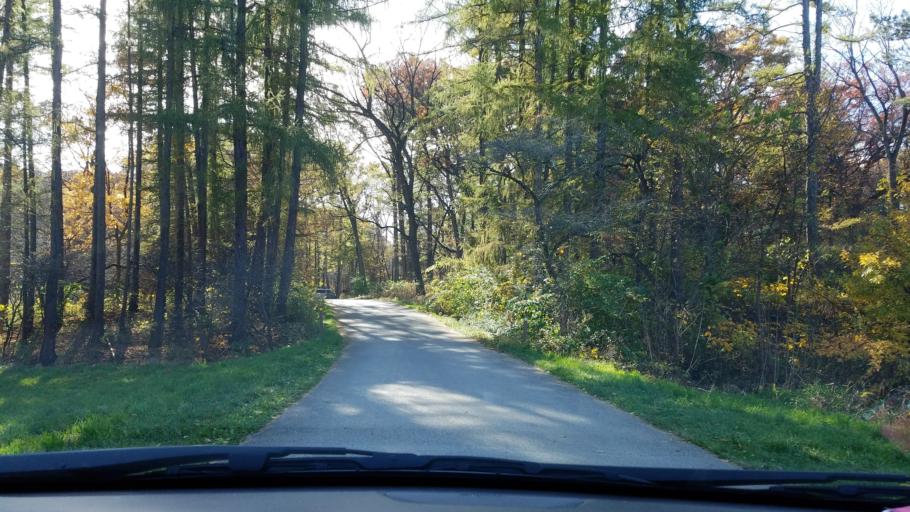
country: US
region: Illinois
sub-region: DuPage County
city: Lisle
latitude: 41.8167
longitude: -88.0842
